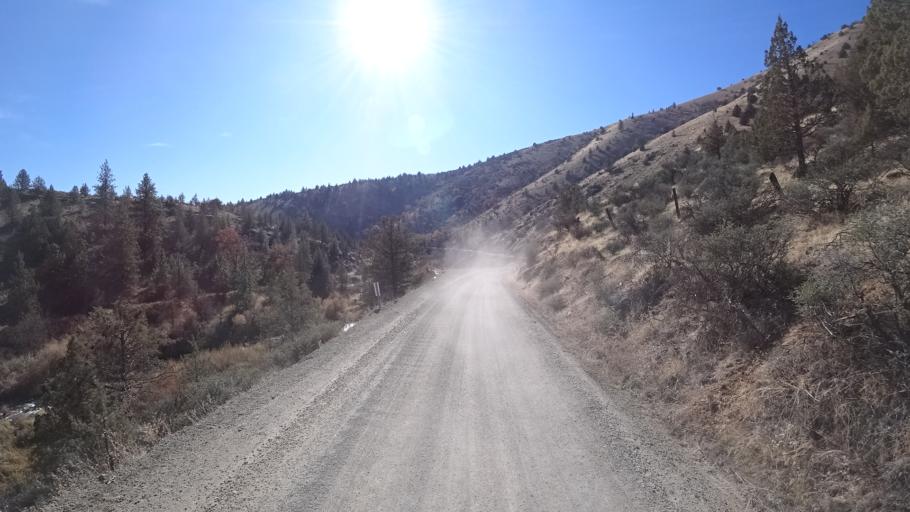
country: US
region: California
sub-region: Siskiyou County
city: Yreka
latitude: 41.7858
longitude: -122.6028
